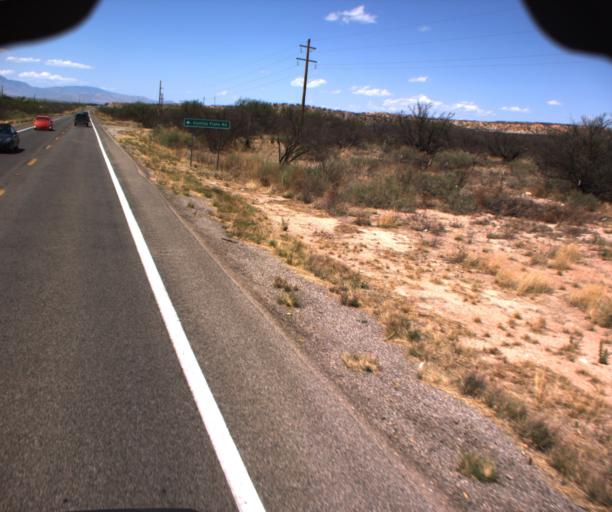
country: US
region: Arizona
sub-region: Cochise County
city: Saint David
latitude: 31.8460
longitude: -110.1945
